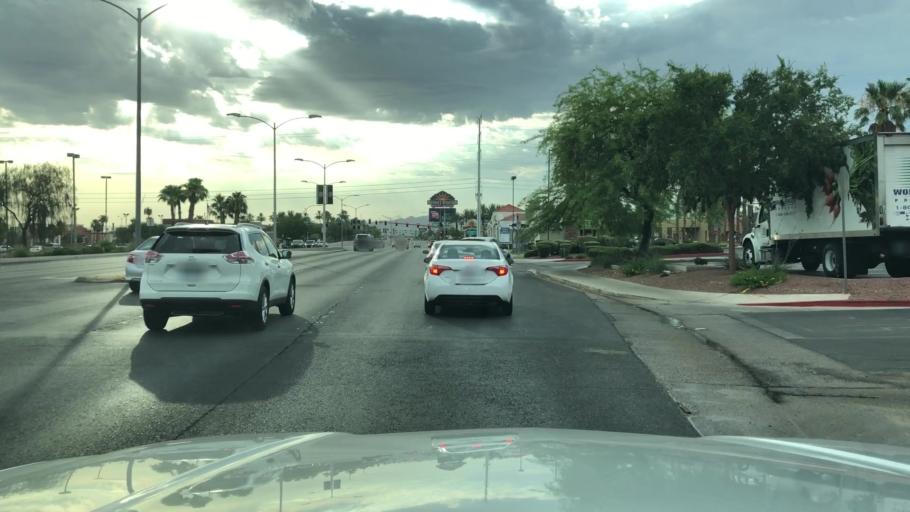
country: US
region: Nevada
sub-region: Clark County
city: Whitney
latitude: 36.0636
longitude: -115.0489
